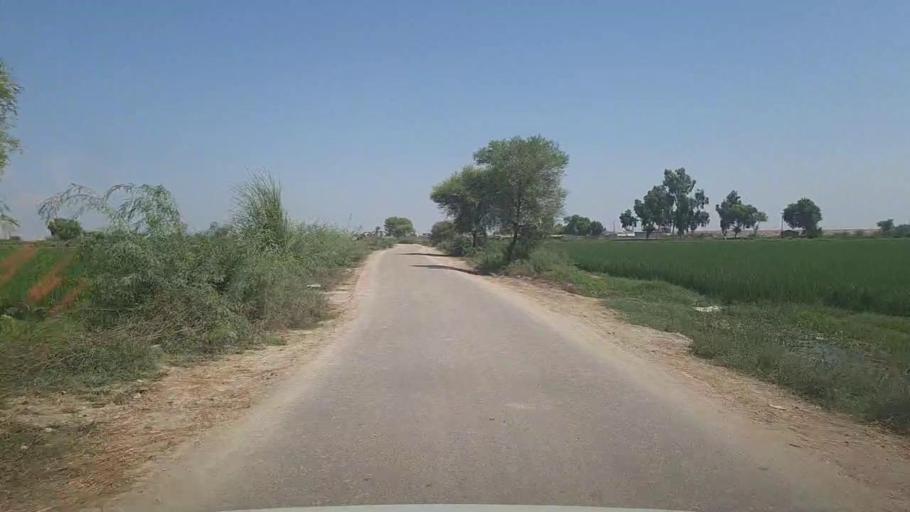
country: PK
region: Sindh
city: Kashmor
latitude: 28.2824
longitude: 69.4399
